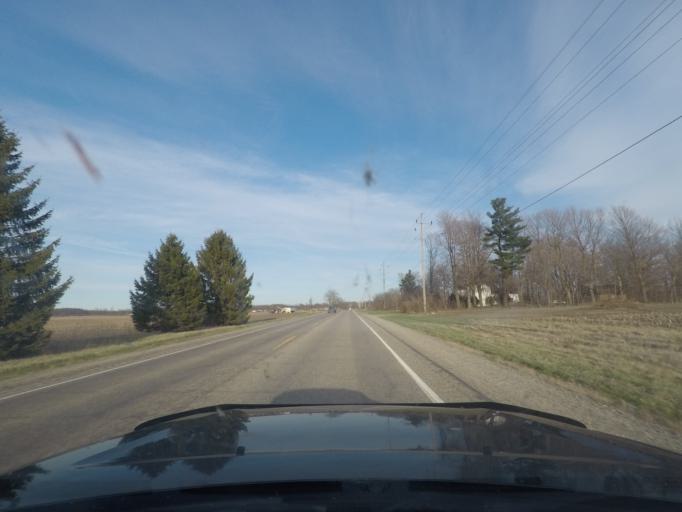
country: US
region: Indiana
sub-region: LaPorte County
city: LaPorte
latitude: 41.5913
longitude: -86.7645
